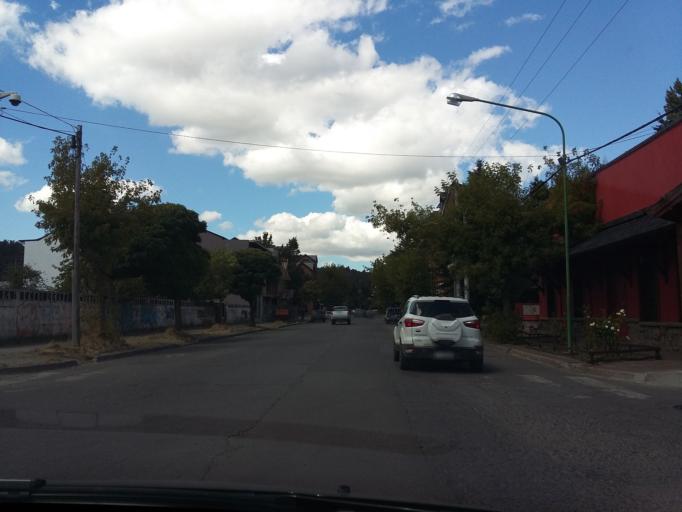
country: AR
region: Neuquen
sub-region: Departamento de Lacar
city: San Martin de los Andes
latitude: -40.1571
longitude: -71.3479
